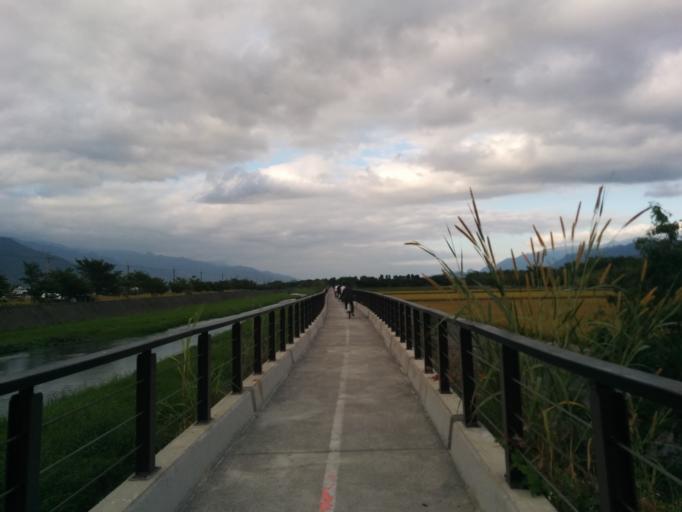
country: TW
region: Taiwan
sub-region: Taitung
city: Taitung
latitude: 23.0299
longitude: 121.1677
